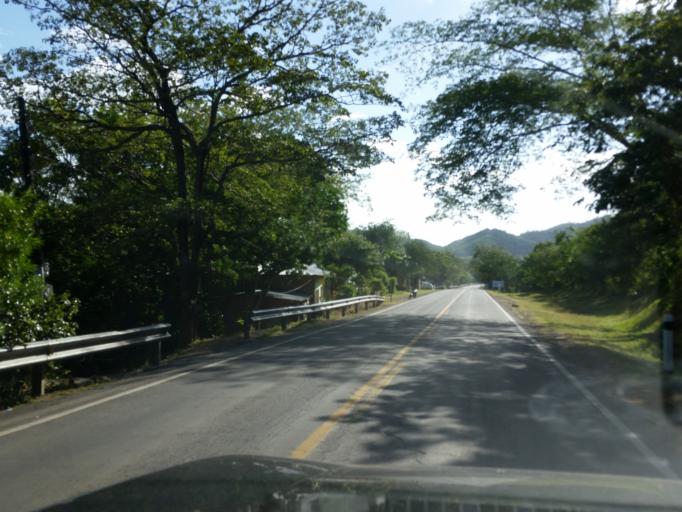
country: NI
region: Rivas
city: San Juan del Sur
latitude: 11.2697
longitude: -85.8460
